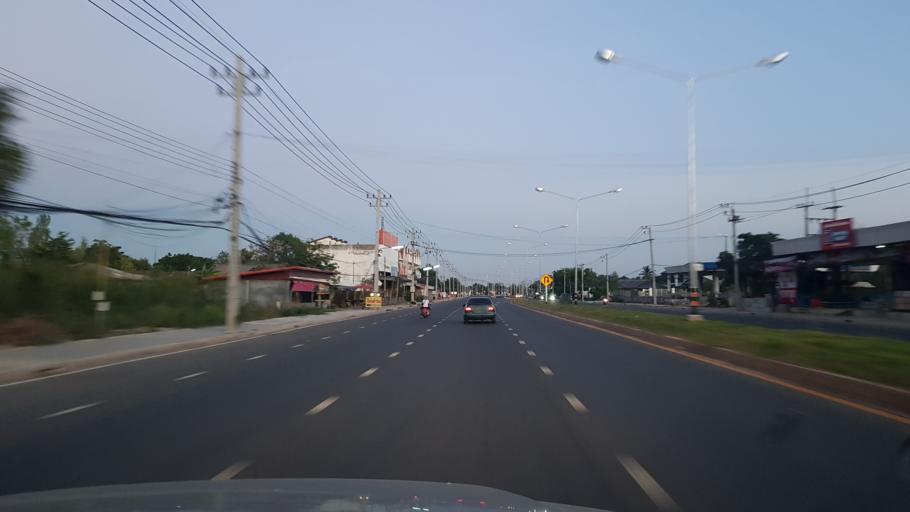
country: TH
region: Chaiyaphum
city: Phu Khiao
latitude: 16.3630
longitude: 102.1432
